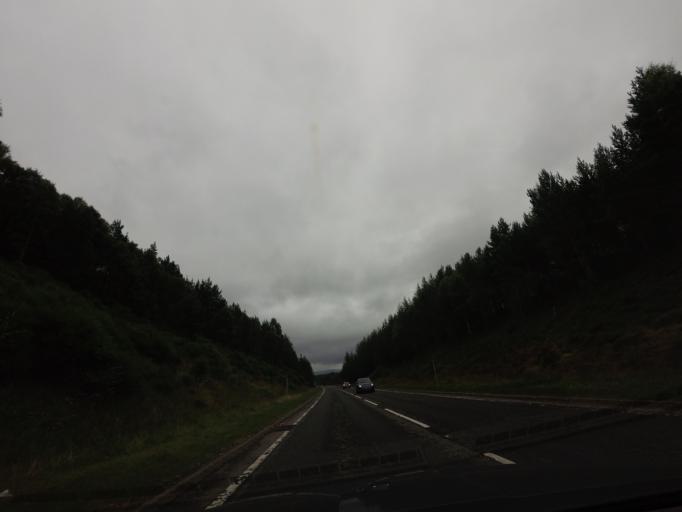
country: GB
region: Scotland
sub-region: Highland
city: Aviemore
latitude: 57.2867
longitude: -3.8428
